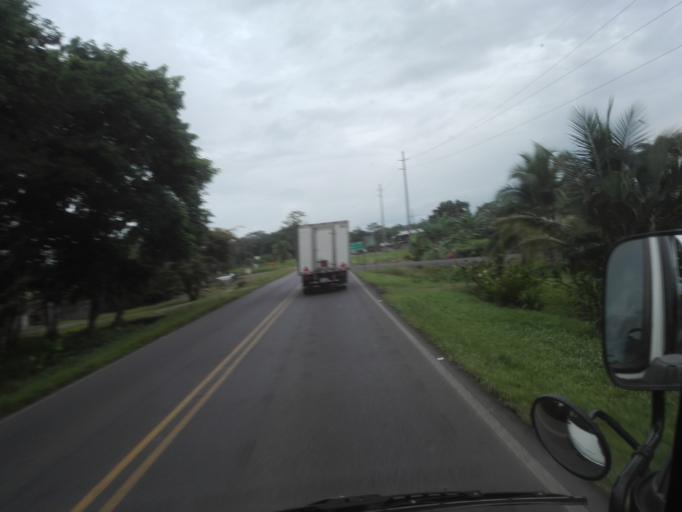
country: CR
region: San Jose
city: Dulce Nombre de Jesus
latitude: 10.3387
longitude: -83.9526
